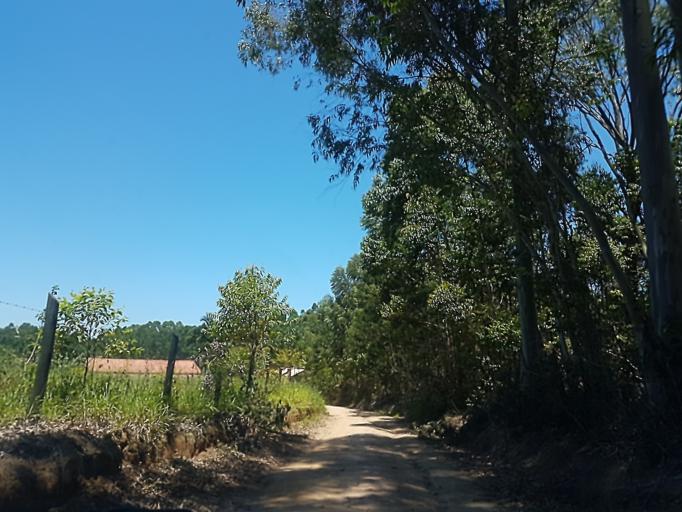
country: BR
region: Santa Catarina
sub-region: Braco Do Norte
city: Braco do Norte
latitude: -28.3952
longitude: -49.1218
